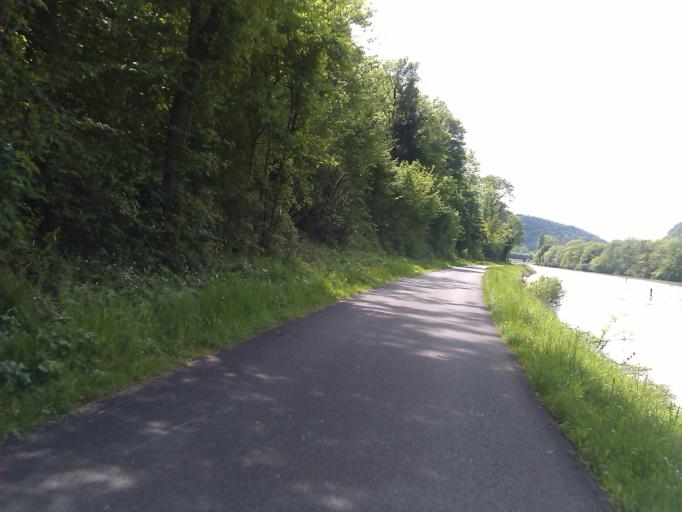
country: FR
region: Franche-Comte
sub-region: Departement du Doubs
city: Montferrand-le-Chateau
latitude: 47.1745
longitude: 5.9401
